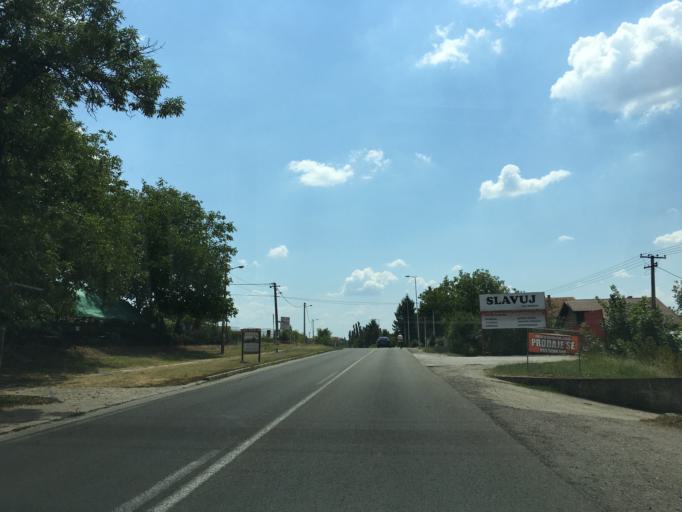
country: RS
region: Central Serbia
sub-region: Belgrade
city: Mladenovac
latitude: 44.4533
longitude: 20.6800
